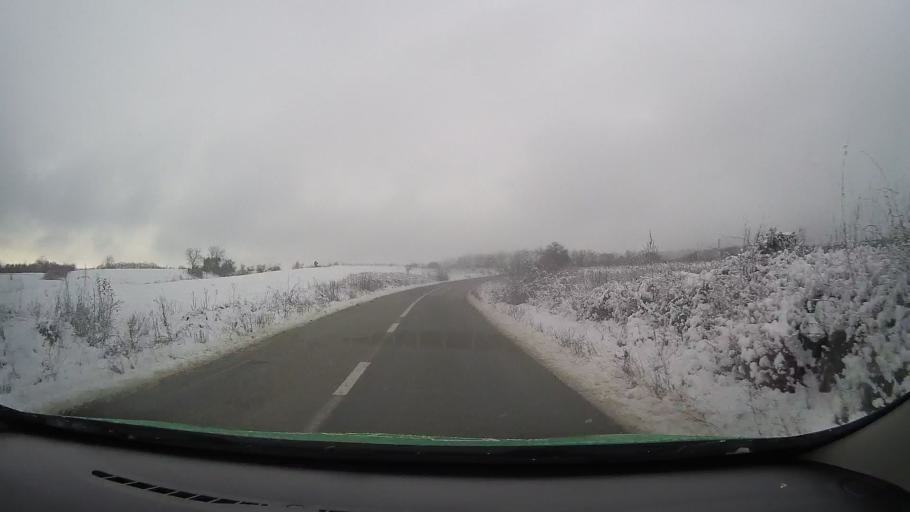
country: RO
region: Hunedoara
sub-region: Oras Hateg
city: Hateg
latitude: 45.6465
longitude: 22.9236
